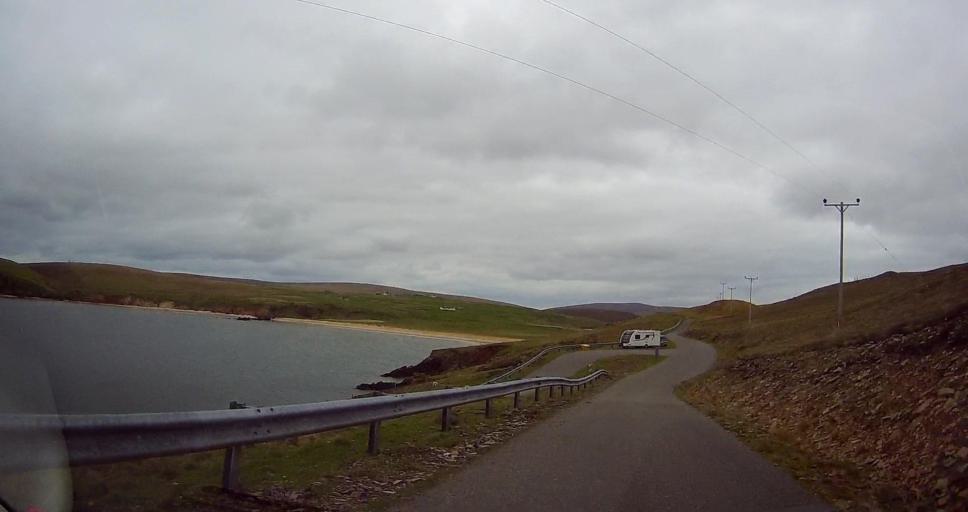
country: GB
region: Scotland
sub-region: Shetland Islands
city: Shetland
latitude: 60.8110
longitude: -0.8768
